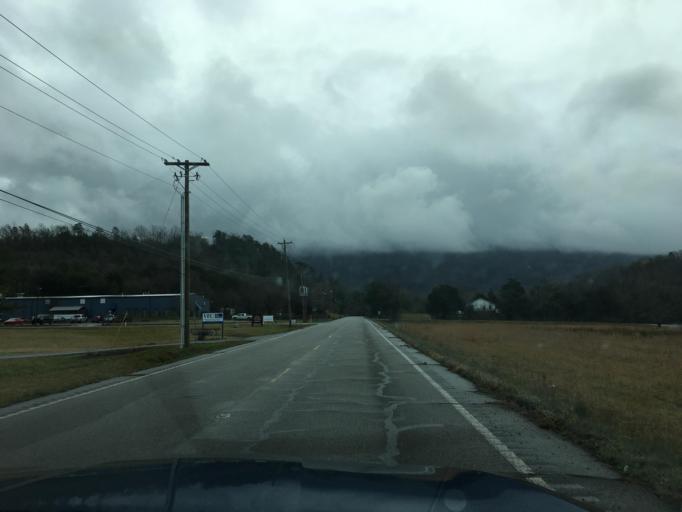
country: US
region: Tennessee
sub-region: Polk County
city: Benton
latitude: 35.1680
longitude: -84.6398
